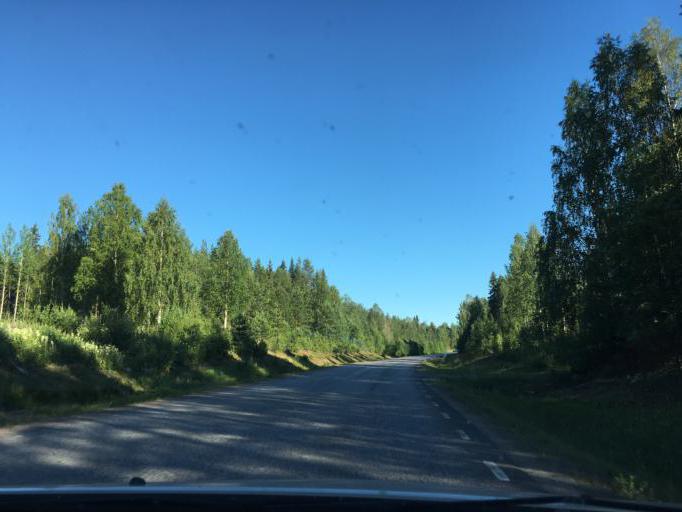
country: SE
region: Norrbotten
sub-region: Kalix Kommun
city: Rolfs
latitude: 65.9147
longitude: 22.9240
